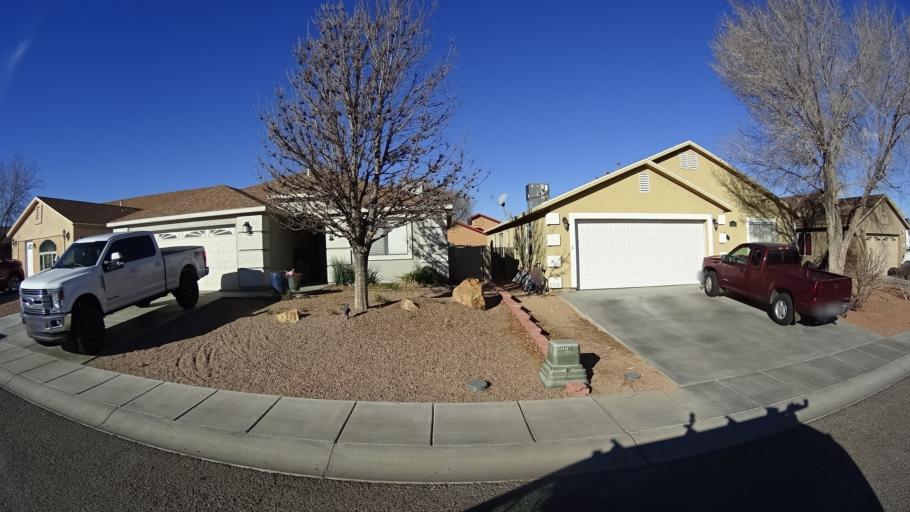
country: US
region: Arizona
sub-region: Mohave County
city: New Kingman-Butler
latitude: 35.2225
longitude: -113.9942
